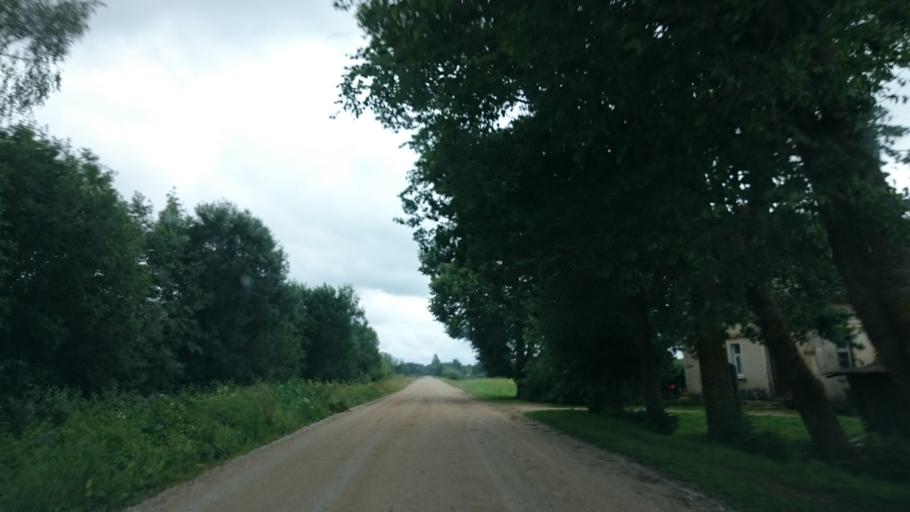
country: LV
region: Durbe
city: Liegi
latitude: 56.7499
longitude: 21.3641
